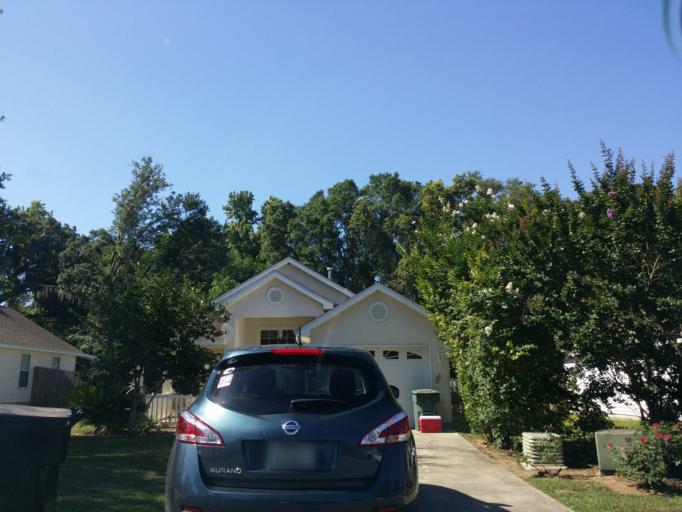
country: US
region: Florida
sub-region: Leon County
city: Tallahassee
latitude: 30.4559
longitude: -84.2145
